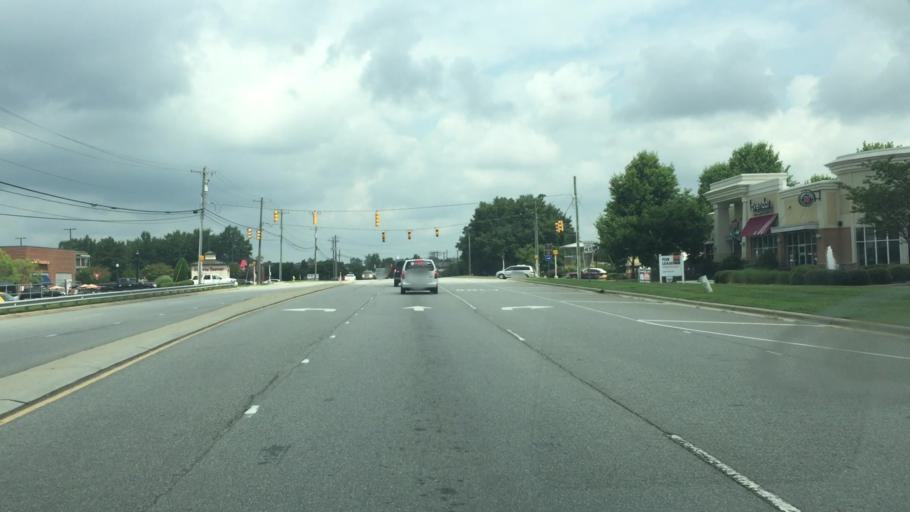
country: US
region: North Carolina
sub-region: Iredell County
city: Mooresville
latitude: 35.5858
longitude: -80.8740
